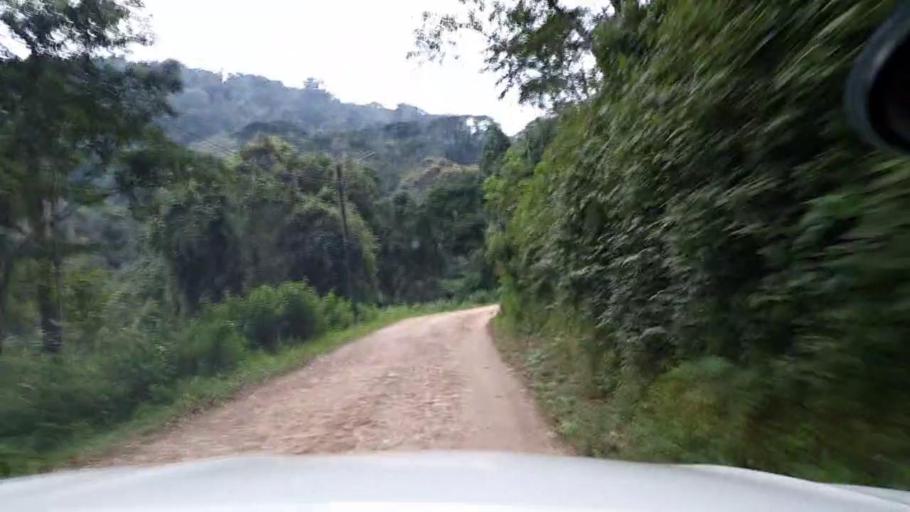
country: RW
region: Southern Province
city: Nzega
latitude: -2.5551
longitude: 29.2337
